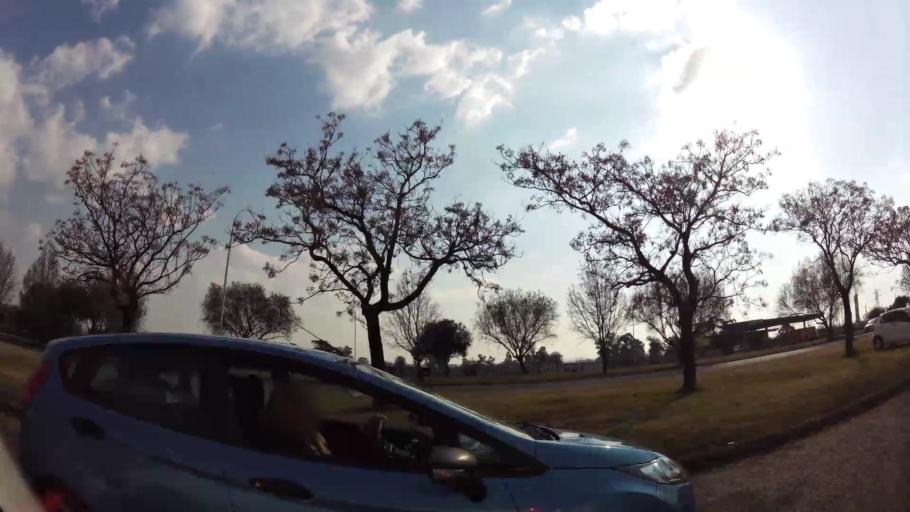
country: ZA
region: Gauteng
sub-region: Ekurhuleni Metropolitan Municipality
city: Boksburg
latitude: -26.2310
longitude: 28.2488
